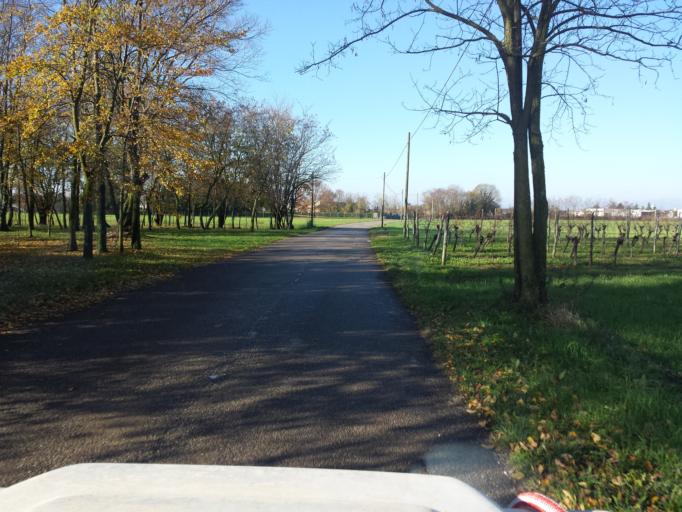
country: IT
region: Friuli Venezia Giulia
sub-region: Provincia di Udine
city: Manzano
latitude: 45.9750
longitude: 13.3731
